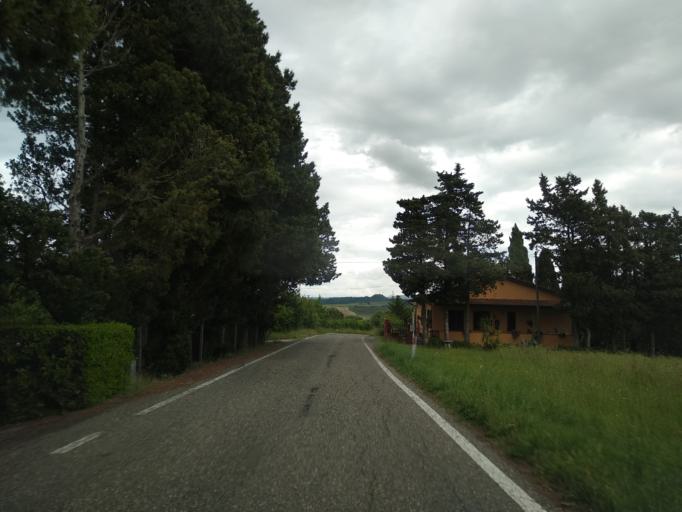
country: IT
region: Tuscany
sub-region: Provincia di Livorno
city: Collesalvetti
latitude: 43.5403
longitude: 10.4539
